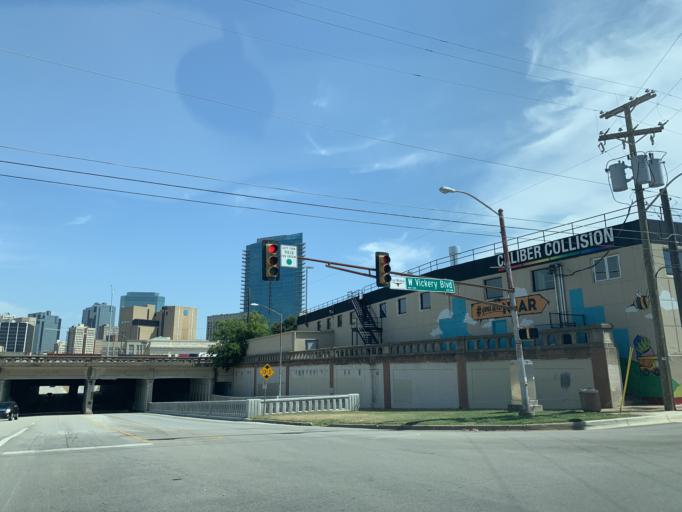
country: US
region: Texas
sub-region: Tarrant County
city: Fort Worth
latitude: 32.7437
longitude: -97.3300
